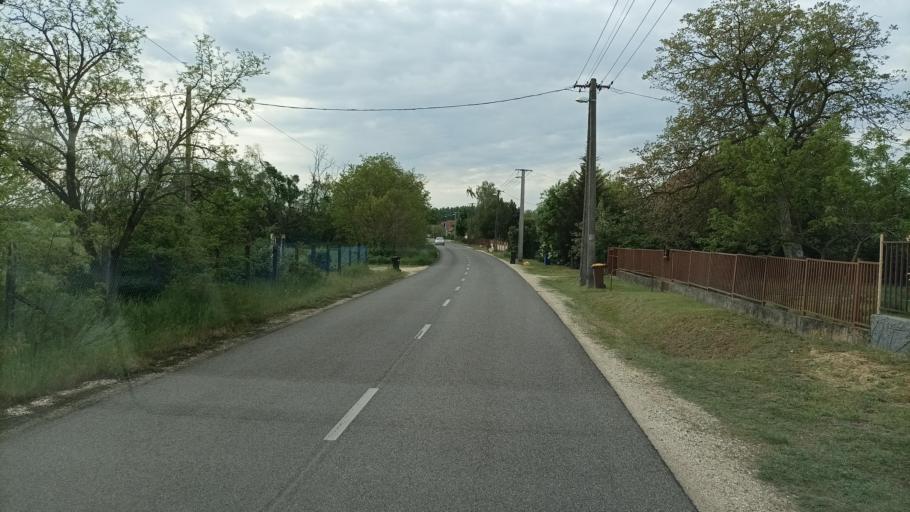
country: HU
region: Pest
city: Monor
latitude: 47.3169
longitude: 19.4120
